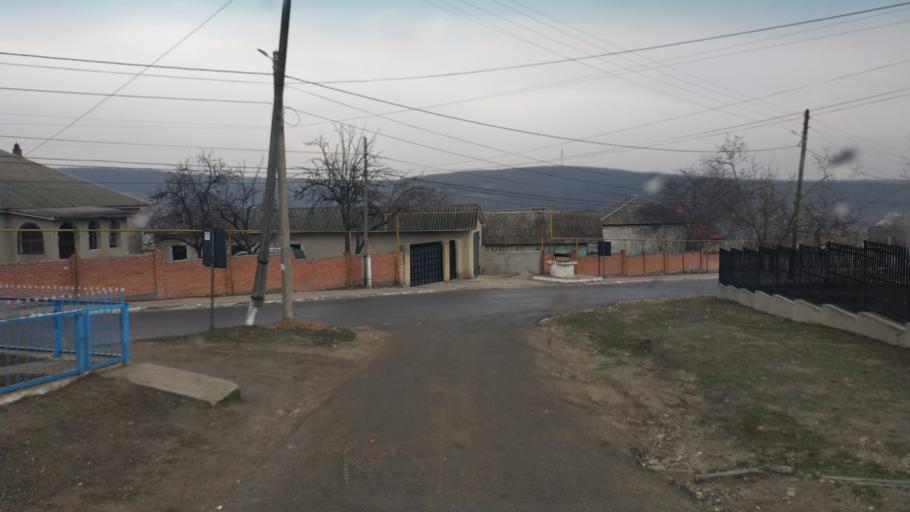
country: MD
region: Chisinau
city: Singera
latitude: 46.8310
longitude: 28.9725
